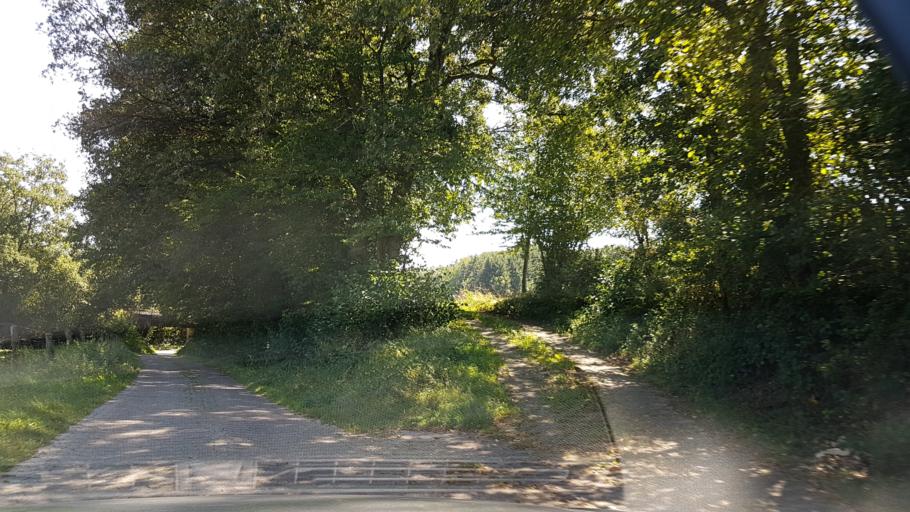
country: DE
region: Rheinland-Pfalz
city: Breitenbach
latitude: 49.4822
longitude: 7.2493
